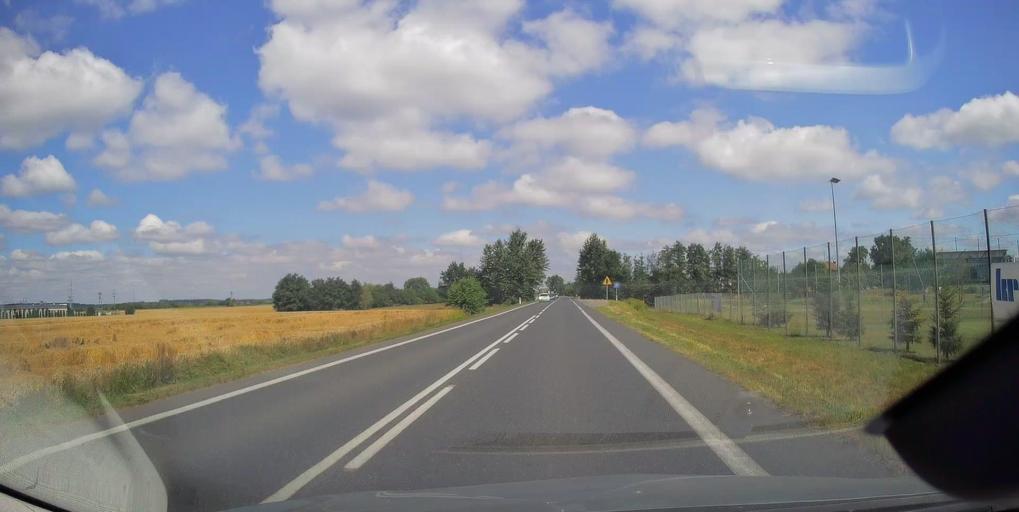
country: PL
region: Subcarpathian Voivodeship
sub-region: Powiat debicki
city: Brzeznica
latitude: 50.1433
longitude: 21.4856
